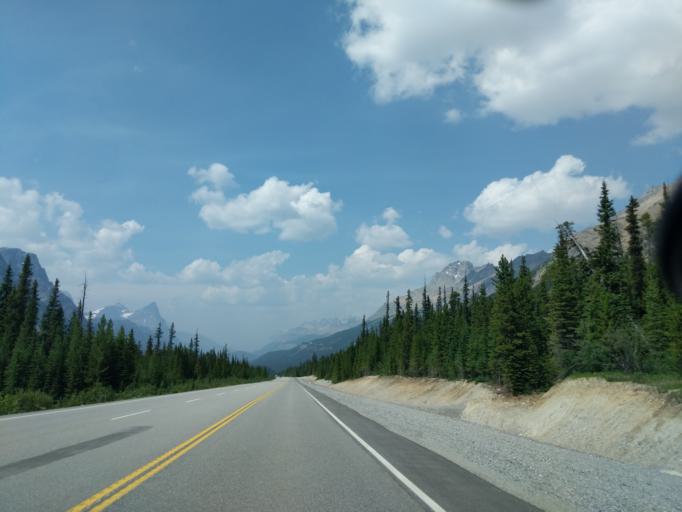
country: CA
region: Alberta
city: Lake Louise
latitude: 51.7315
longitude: -116.5033
